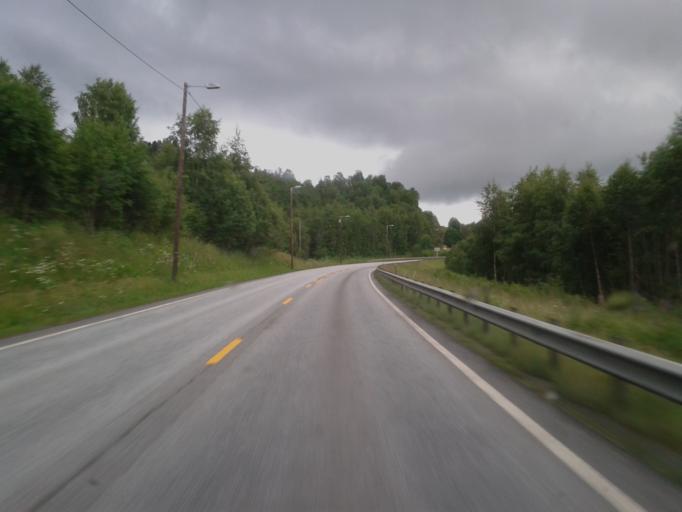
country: NO
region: Sor-Trondelag
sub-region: Melhus
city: Lundamo
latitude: 63.1150
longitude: 10.2419
